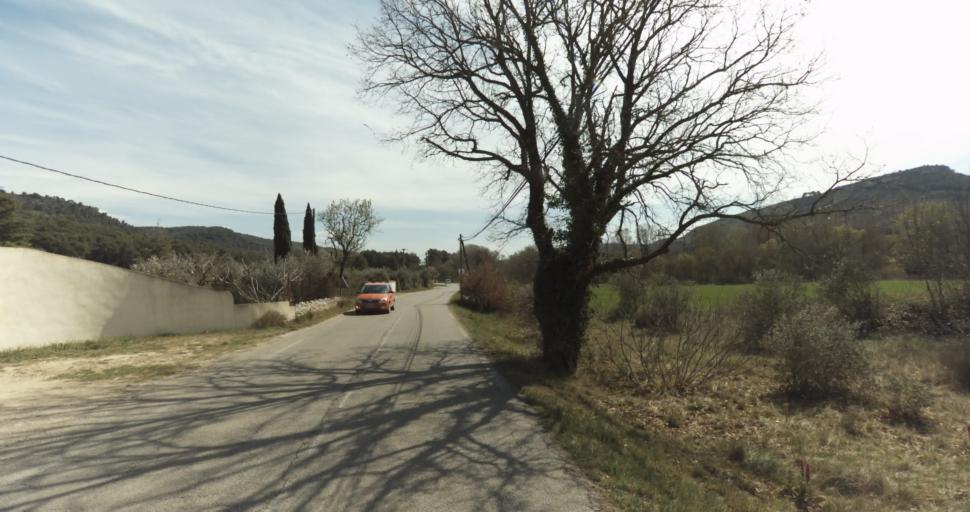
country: FR
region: Provence-Alpes-Cote d'Azur
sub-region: Departement des Bouches-du-Rhone
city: Ventabren
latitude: 43.5335
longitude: 5.2804
